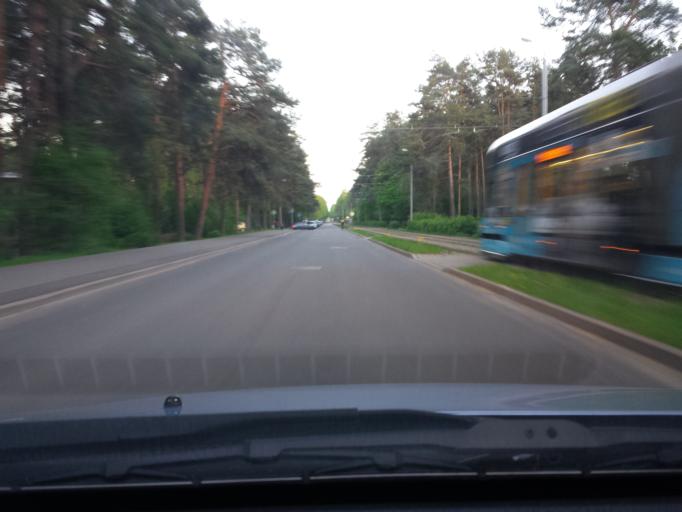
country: LV
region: Riga
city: Jaunciems
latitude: 57.0040
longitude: 24.1576
